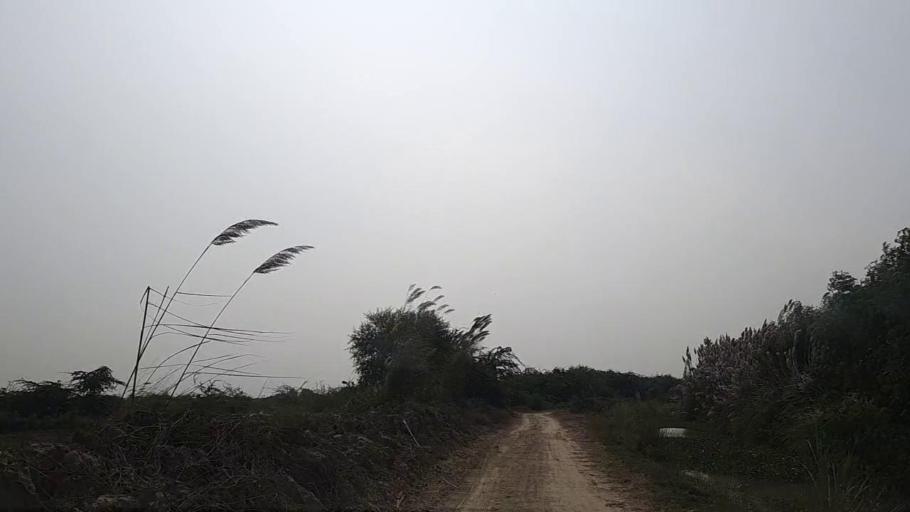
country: PK
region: Sindh
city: Mirpur Sakro
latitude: 24.6510
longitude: 67.7673
